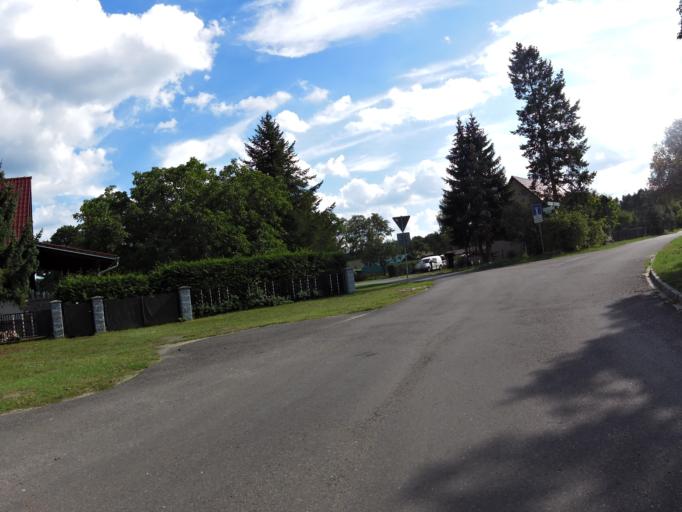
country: DE
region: Brandenburg
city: Munchehofe
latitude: 52.1921
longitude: 13.8773
